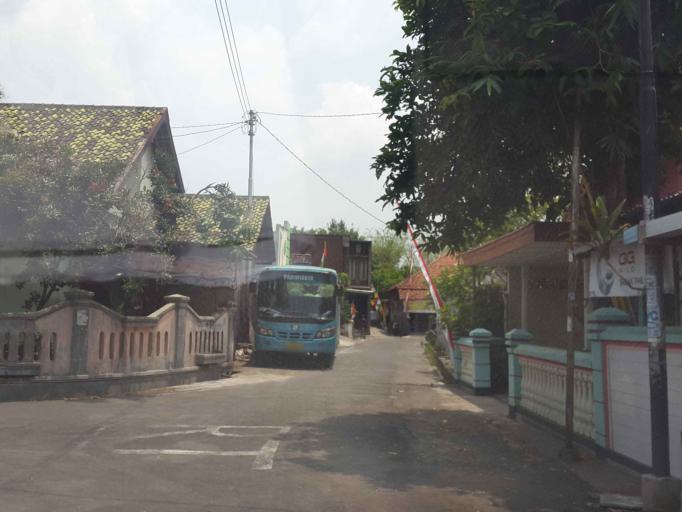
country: ID
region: Central Java
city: Jaten
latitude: -7.5894
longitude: 110.9348
